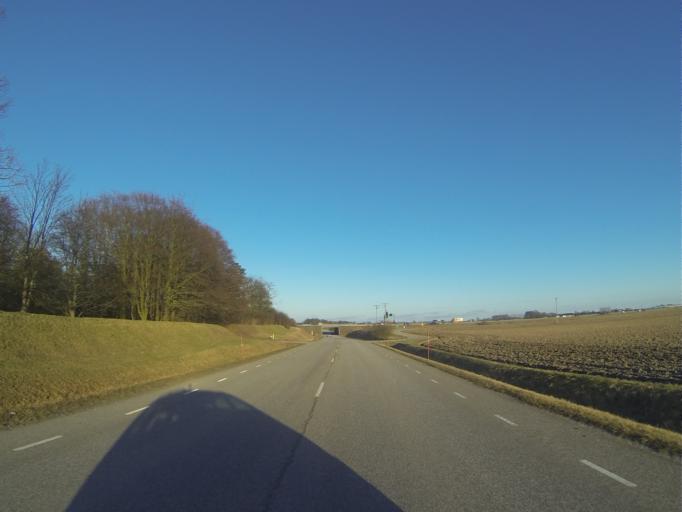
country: SE
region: Skane
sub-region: Malmo
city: Tygelsjo
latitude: 55.5431
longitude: 13.0009
